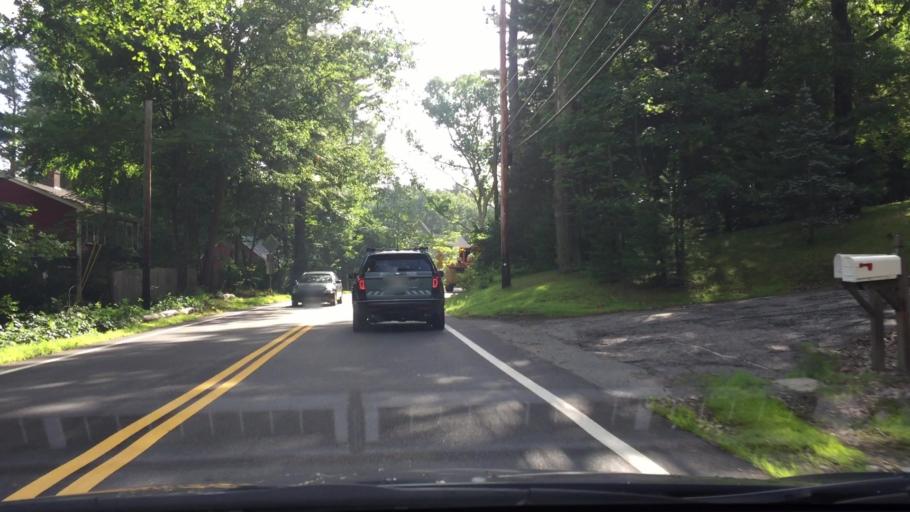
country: US
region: Massachusetts
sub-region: Middlesex County
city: Stow
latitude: 42.4806
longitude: -71.5008
